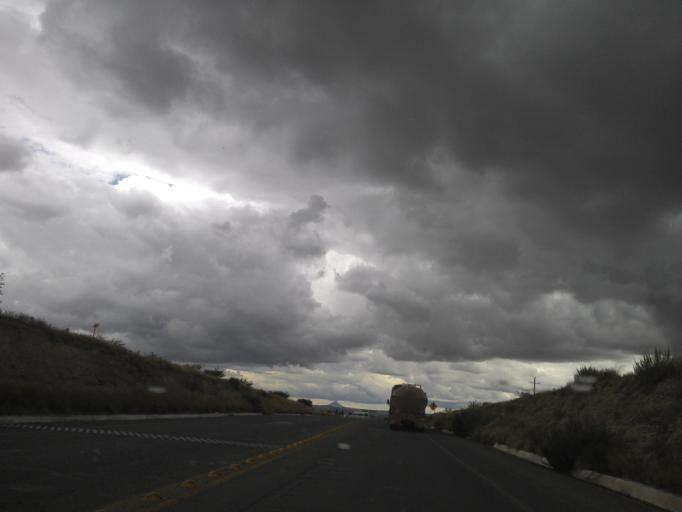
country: MX
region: Zacatecas
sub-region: Rio Grande
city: Los Condes
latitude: 23.8685
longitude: -103.0821
